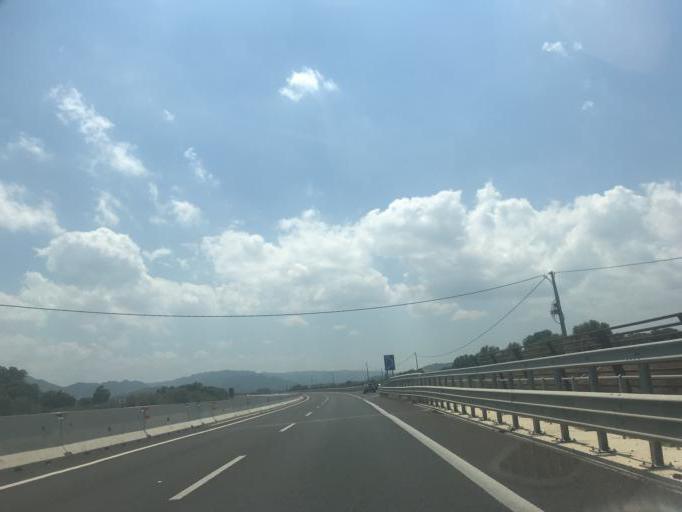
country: IT
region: Sardinia
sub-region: Provincia di Olbia-Tempio
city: Loiri Porto San Paolo
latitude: 40.8821
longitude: 9.4691
